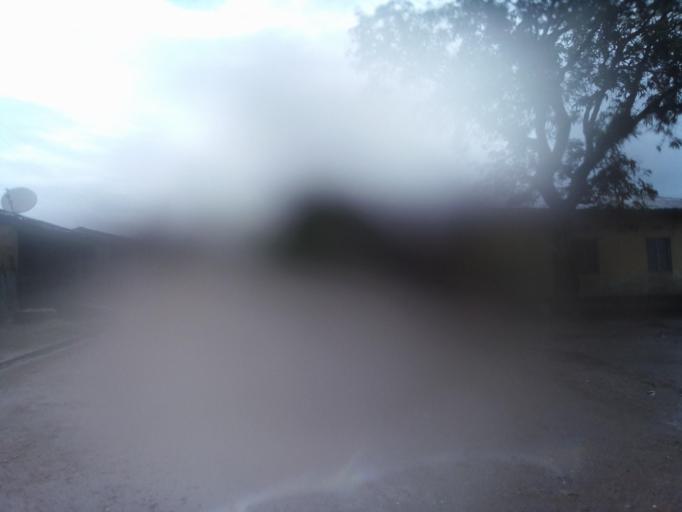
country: SL
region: Eastern Province
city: Kenema
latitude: 7.8817
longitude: -11.1835
